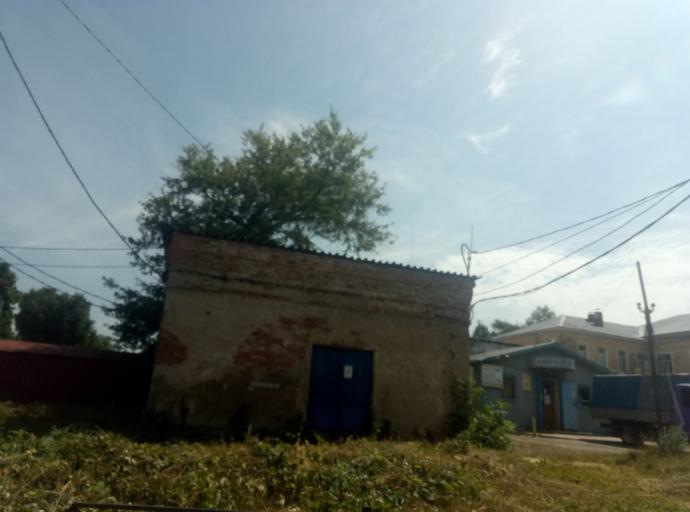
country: RU
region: Tula
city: Kireyevsk
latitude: 53.9307
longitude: 37.9329
